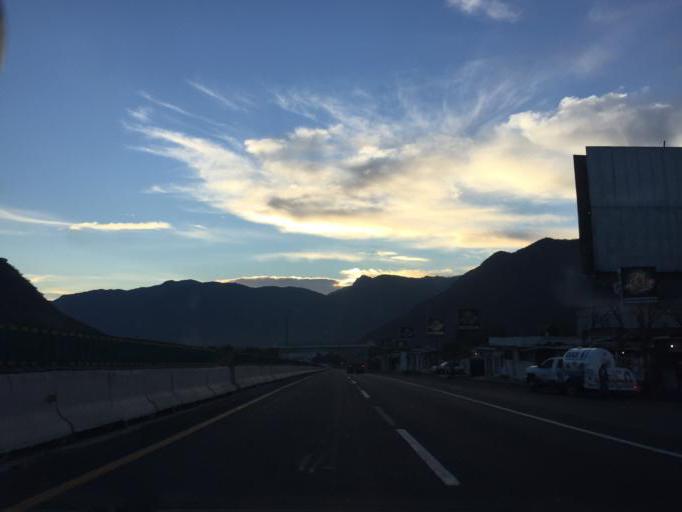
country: MX
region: Veracruz
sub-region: Nogales
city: Agricola Lazaro Cardenas
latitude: 18.8190
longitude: -97.2271
